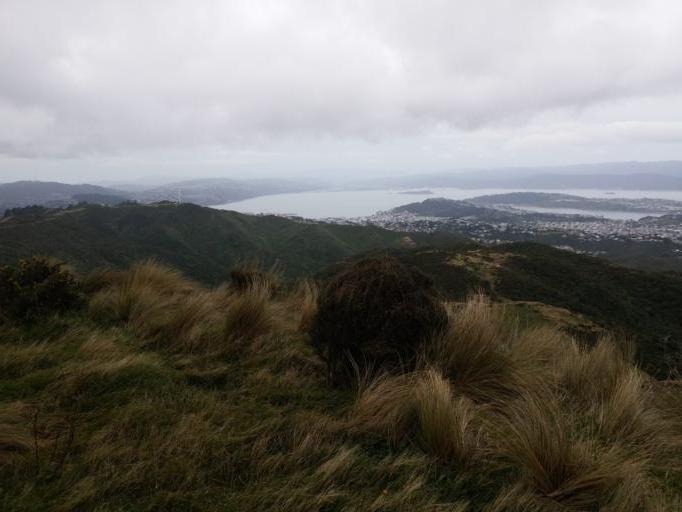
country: NZ
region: Wellington
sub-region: Wellington City
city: Brooklyn
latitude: -41.3259
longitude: 174.7324
